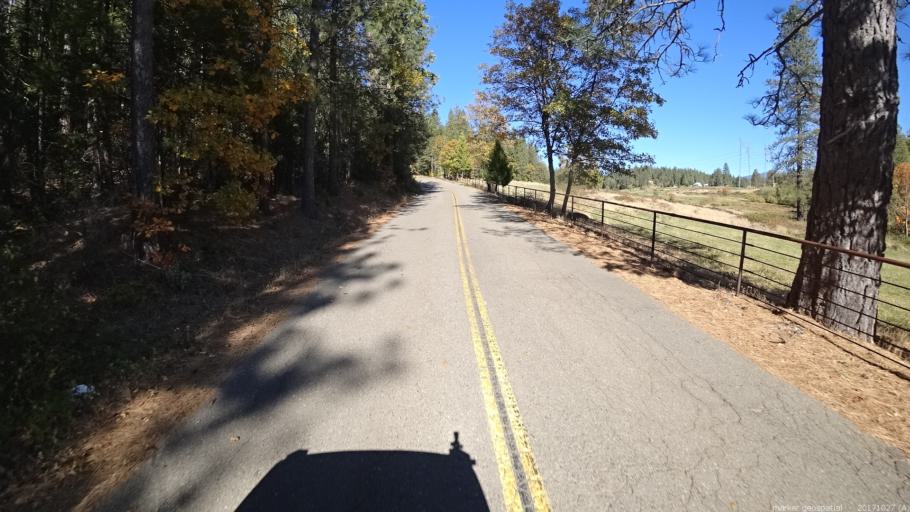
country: US
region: California
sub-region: Shasta County
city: Shingletown
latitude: 40.7145
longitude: -121.9452
